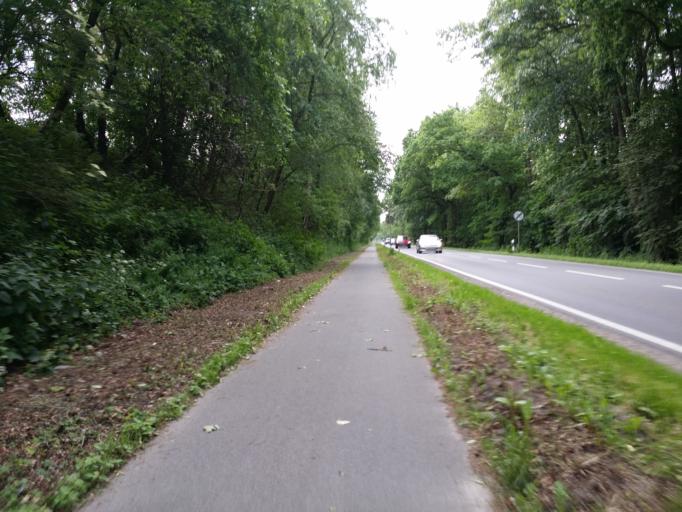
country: DE
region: Lower Saxony
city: Wittmund
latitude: 53.5610
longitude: 7.7842
